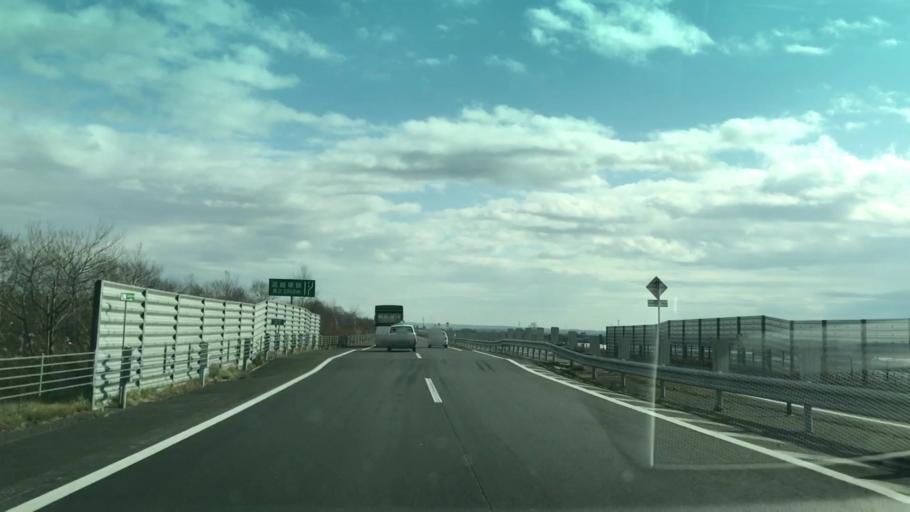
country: JP
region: Hokkaido
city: Tomakomai
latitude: 42.5928
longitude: 141.9143
